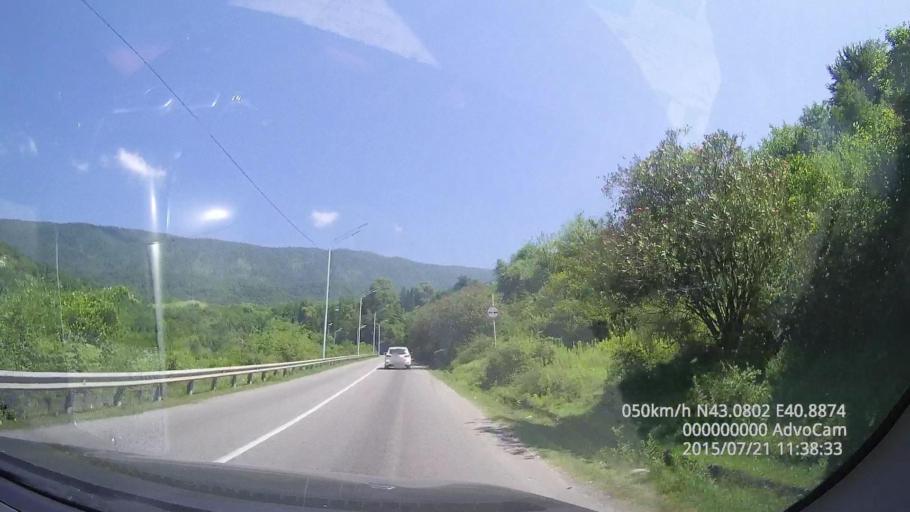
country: GE
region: Abkhazia
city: Stantsiya Novyy Afon
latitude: 43.0805
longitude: 40.8875
